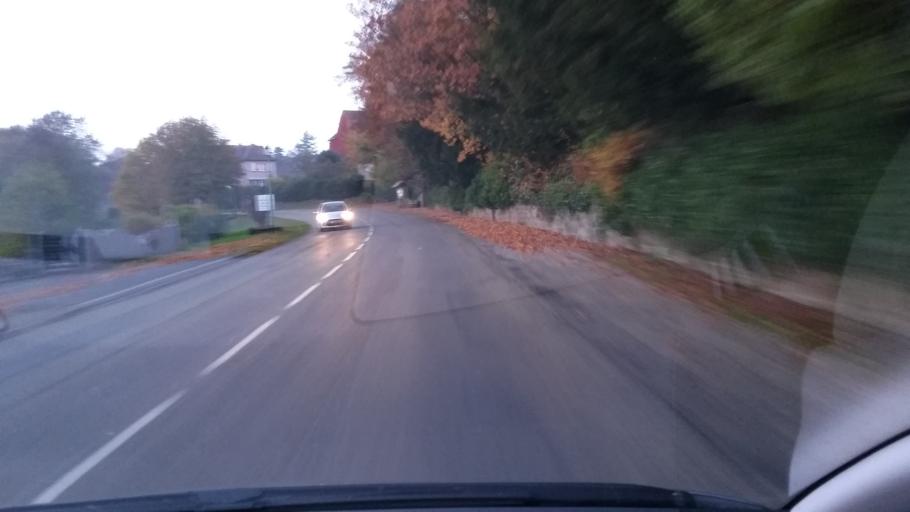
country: FR
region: Alsace
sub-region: Departement du Bas-Rhin
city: Neuwiller-les-Saverne
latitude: 48.8632
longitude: 7.3185
